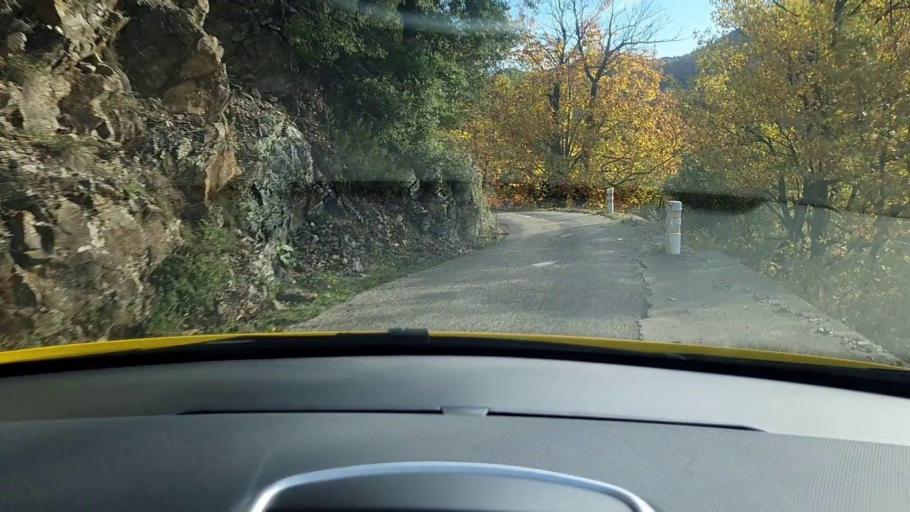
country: FR
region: Languedoc-Roussillon
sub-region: Departement du Gard
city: Valleraugue
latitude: 44.0855
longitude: 3.7407
